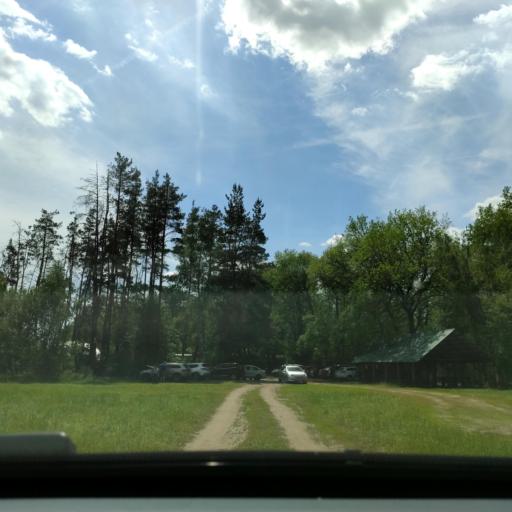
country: RU
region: Voronezj
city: Podgornoye
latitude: 51.8057
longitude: 39.1493
